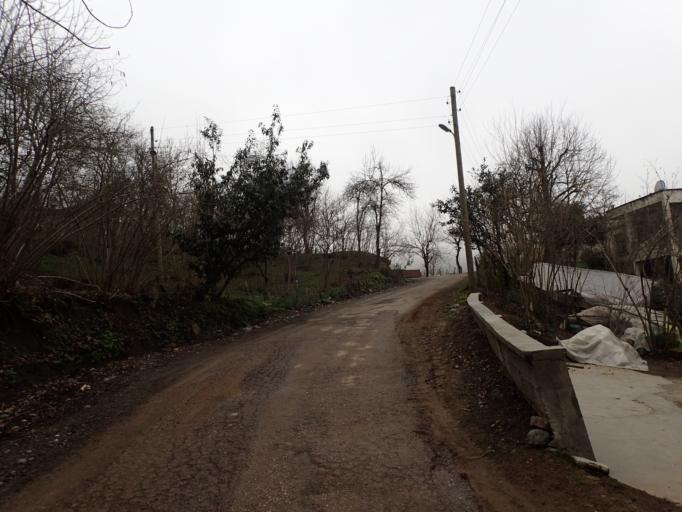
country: TR
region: Ordu
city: Camas
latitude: 40.9294
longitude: 37.5514
